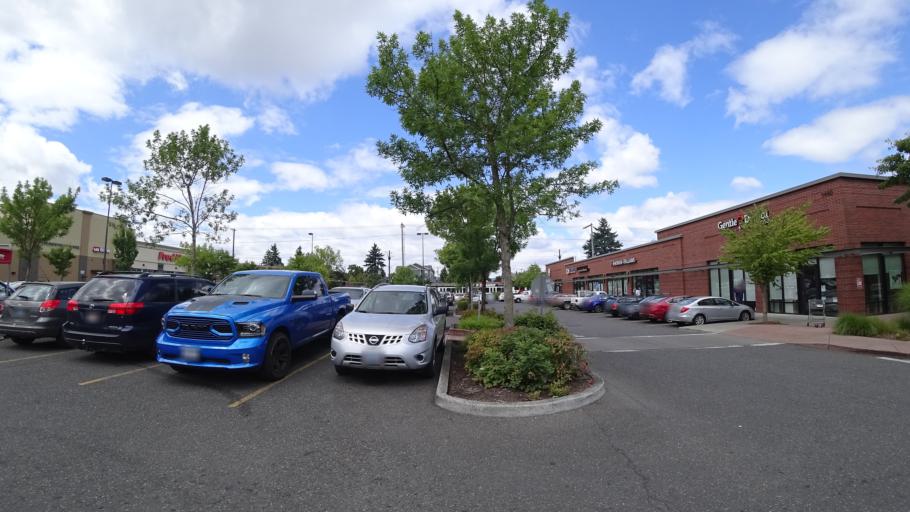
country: US
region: Oregon
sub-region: Multnomah County
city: Portland
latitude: 45.5767
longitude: -122.6810
